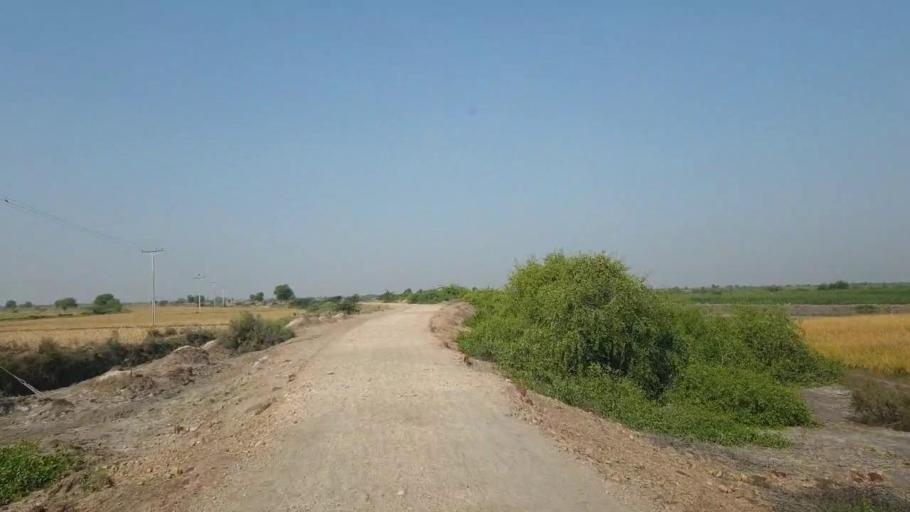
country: PK
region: Sindh
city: Badin
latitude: 24.5189
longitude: 68.7787
